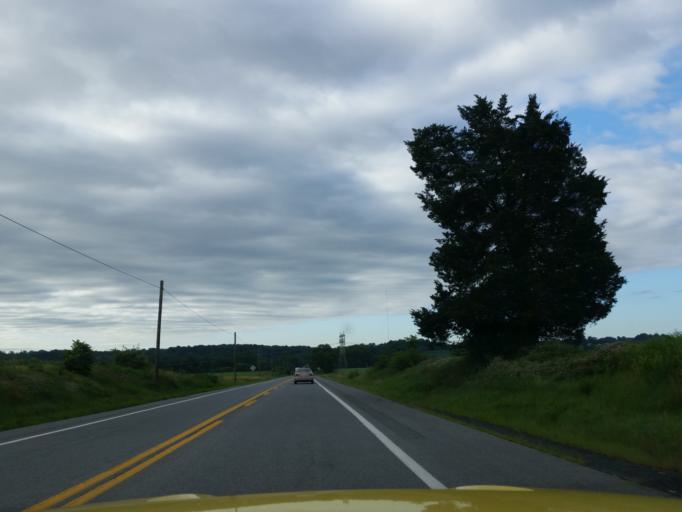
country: US
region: Pennsylvania
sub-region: Lancaster County
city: Elizabethtown
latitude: 40.1960
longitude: -76.6079
